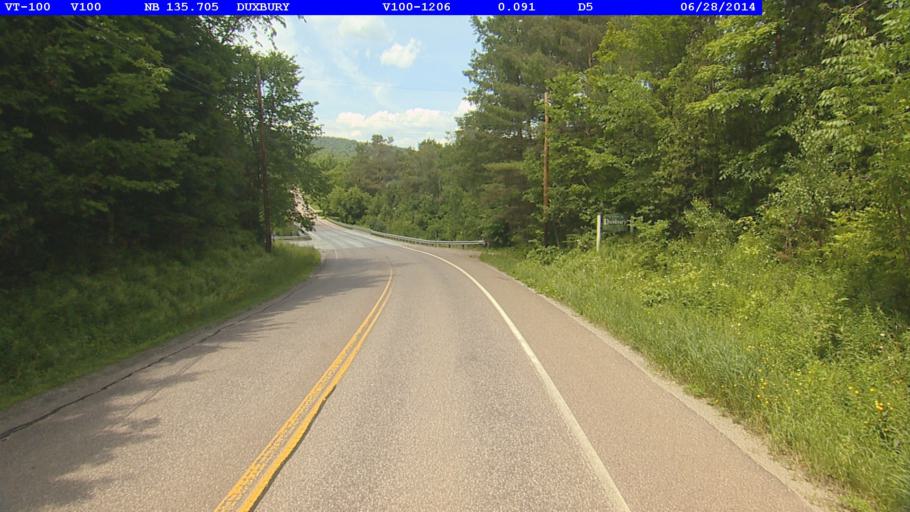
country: US
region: Vermont
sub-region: Washington County
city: Waterbury
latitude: 44.2480
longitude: -72.7859
